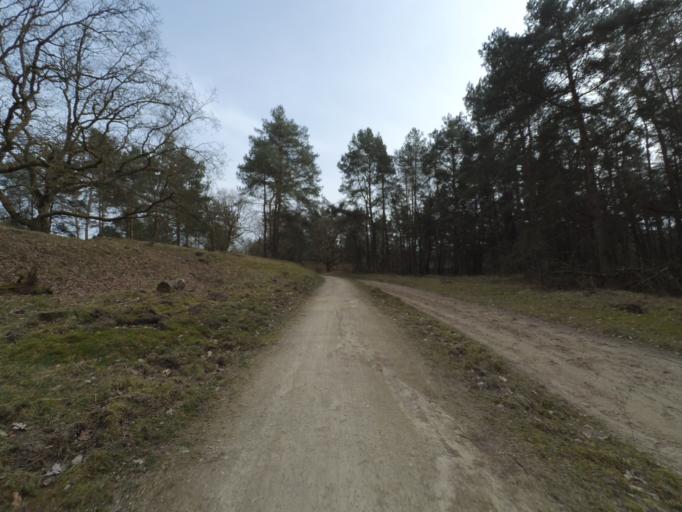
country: NL
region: Gelderland
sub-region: Gemeente Renkum
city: Wolfheze
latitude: 52.0488
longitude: 5.7720
